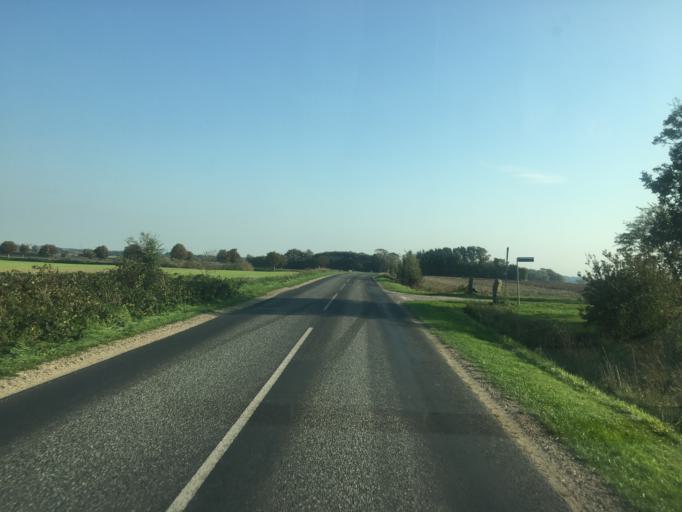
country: DE
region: Schleswig-Holstein
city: Bramstedtlund
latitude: 54.9505
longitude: 9.0580
